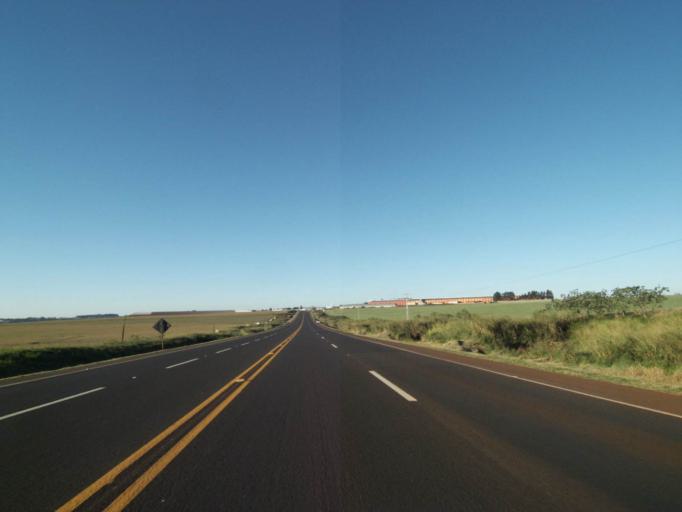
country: BR
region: Parana
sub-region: Arapongas
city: Arapongas
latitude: -23.4162
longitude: -51.4774
